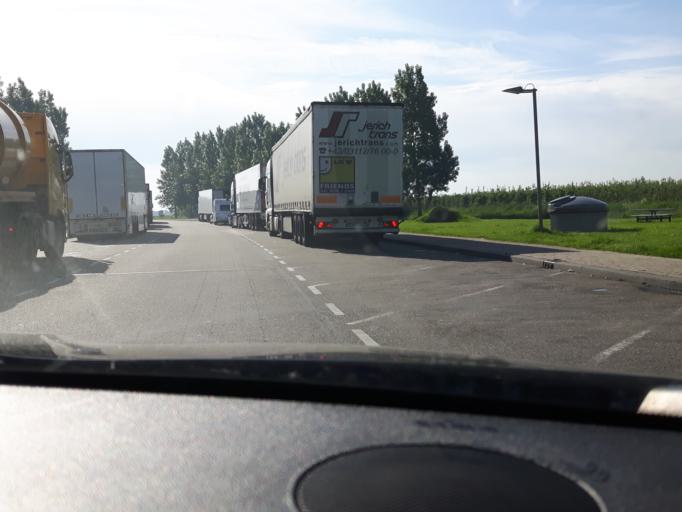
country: NL
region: Zeeland
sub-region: Gemeente Reimerswaal
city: Yerseke
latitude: 51.4248
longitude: 4.0885
